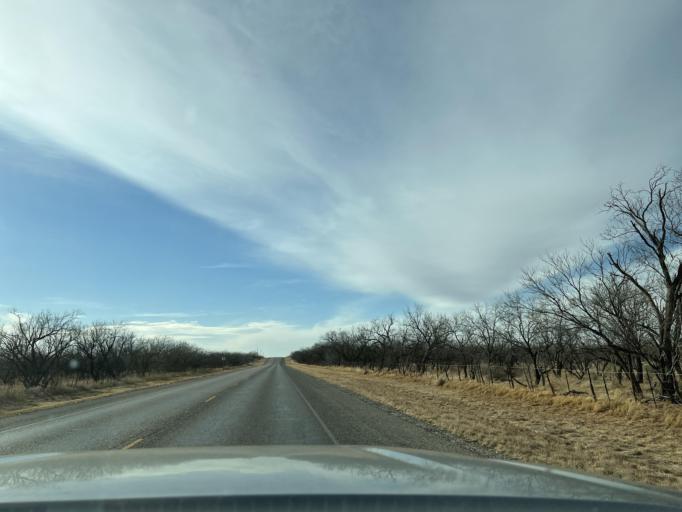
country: US
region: Texas
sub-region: Fisher County
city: Rotan
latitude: 32.7396
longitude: -100.5207
